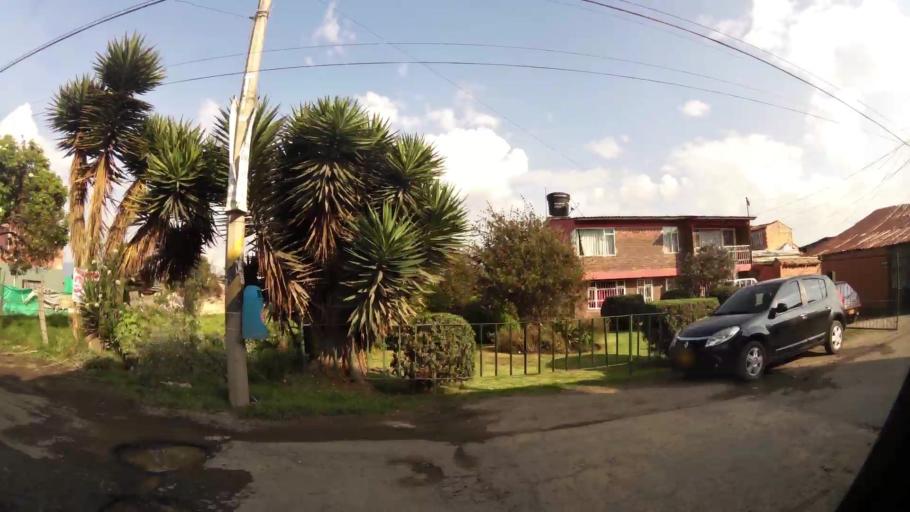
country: CO
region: Cundinamarca
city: Cota
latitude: 4.8033
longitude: -74.1008
